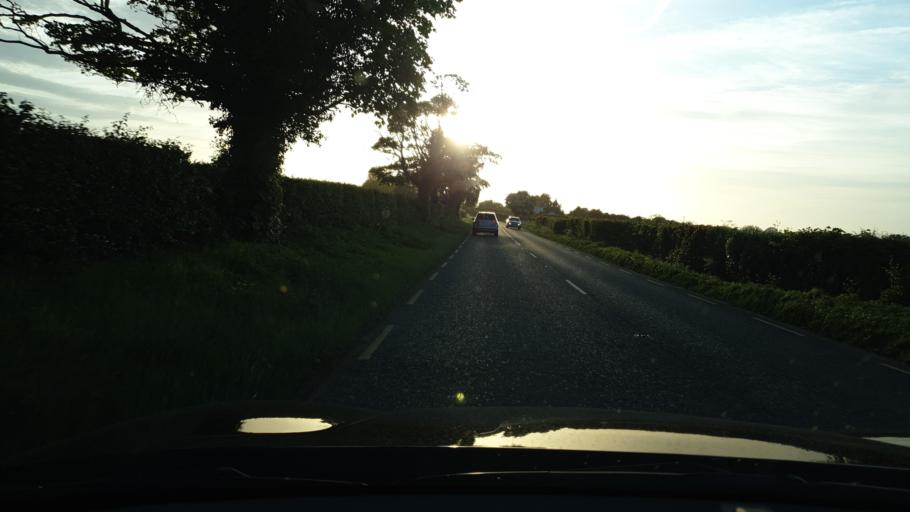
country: IE
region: Leinster
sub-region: An Mhi
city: Ratoath
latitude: 53.5015
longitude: -6.4344
